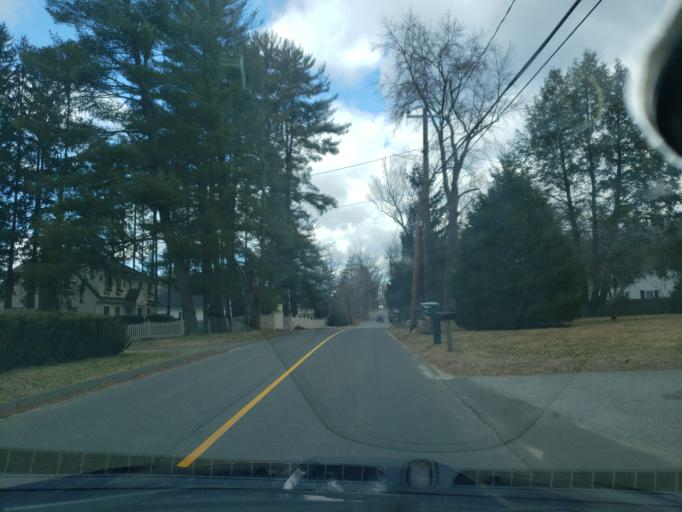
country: US
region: Connecticut
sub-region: Fairfield County
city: Bethel
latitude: 41.3839
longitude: -73.3762
